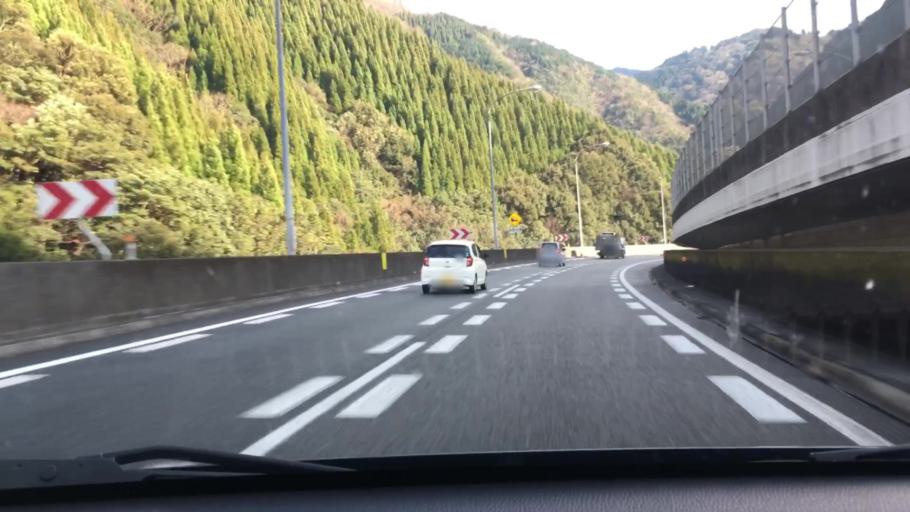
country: JP
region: Kumamoto
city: Hitoyoshi
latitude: 32.3265
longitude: 130.7565
